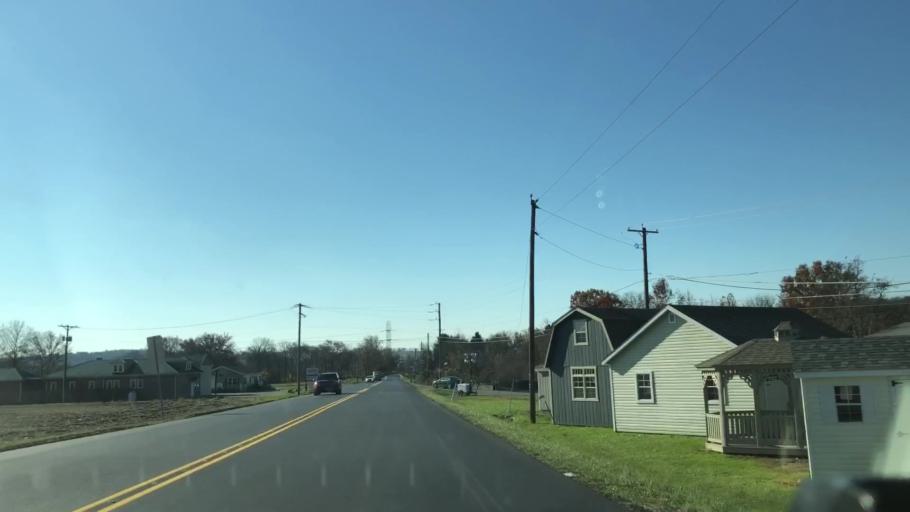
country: US
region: Pennsylvania
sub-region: Berks County
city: Bally
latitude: 40.4463
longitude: -75.5534
